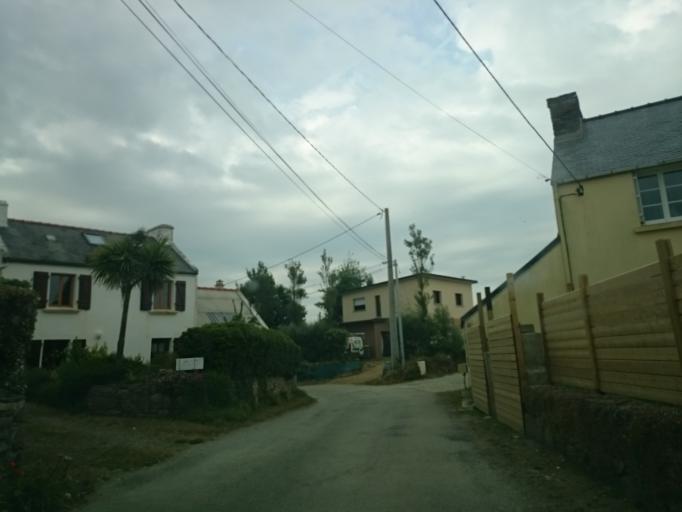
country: FR
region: Brittany
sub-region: Departement du Finistere
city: Le Conquet
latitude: 48.4034
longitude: -4.7666
